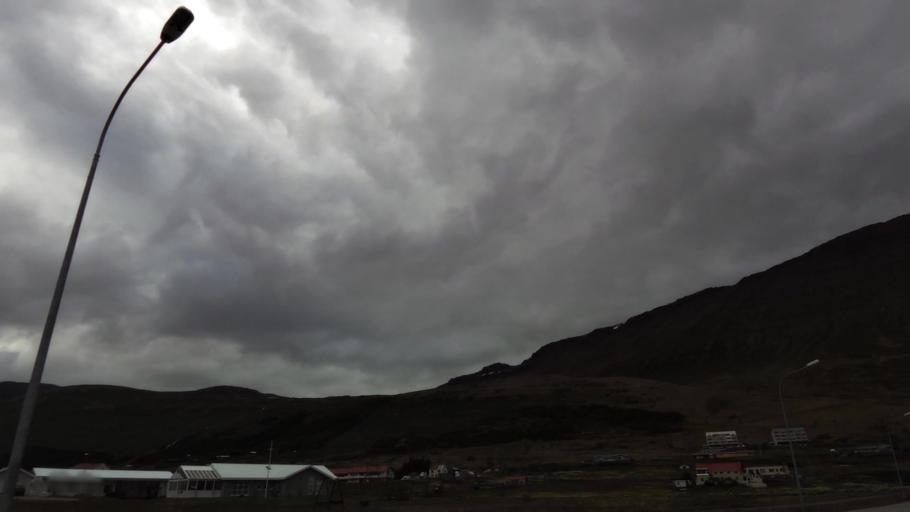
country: IS
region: Westfjords
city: Isafjoerdur
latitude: 66.0599
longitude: -23.1761
